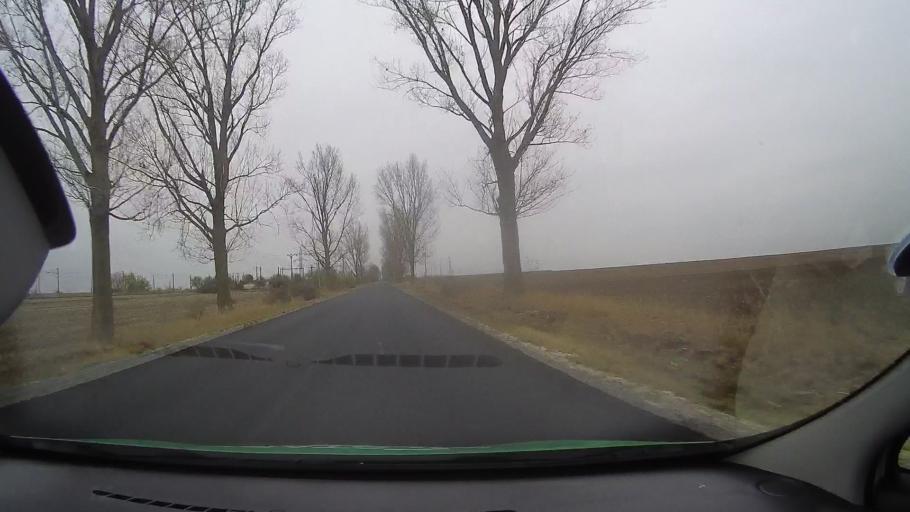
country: RO
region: Ialomita
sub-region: Comuna Valea Ciorii
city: Valea Ciorii
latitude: 44.7494
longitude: 27.5698
